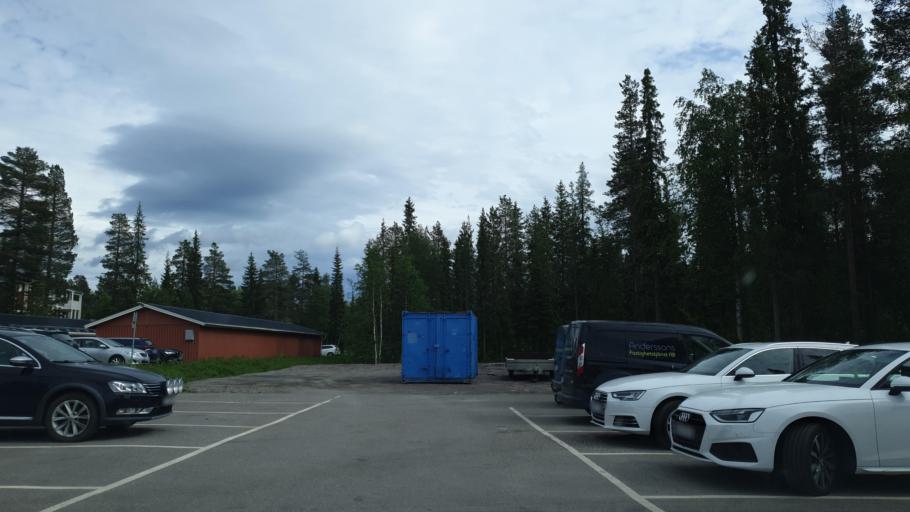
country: SE
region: Norrbotten
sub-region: Gallivare Kommun
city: Gaellivare
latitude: 67.1245
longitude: 20.6616
